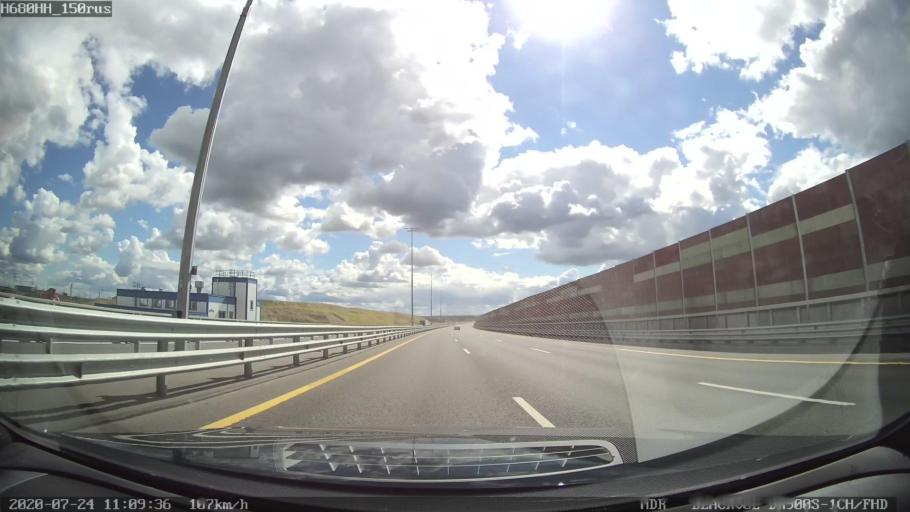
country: RU
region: St.-Petersburg
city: Tyarlevo
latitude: 59.7482
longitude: 30.4795
